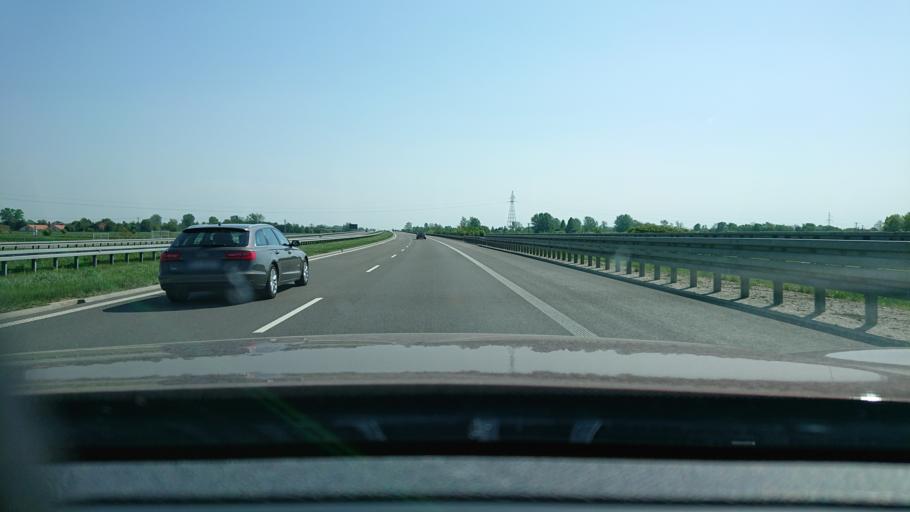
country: PL
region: Subcarpathian Voivodeship
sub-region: Powiat lancucki
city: Lancut
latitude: 50.0984
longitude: 22.2422
